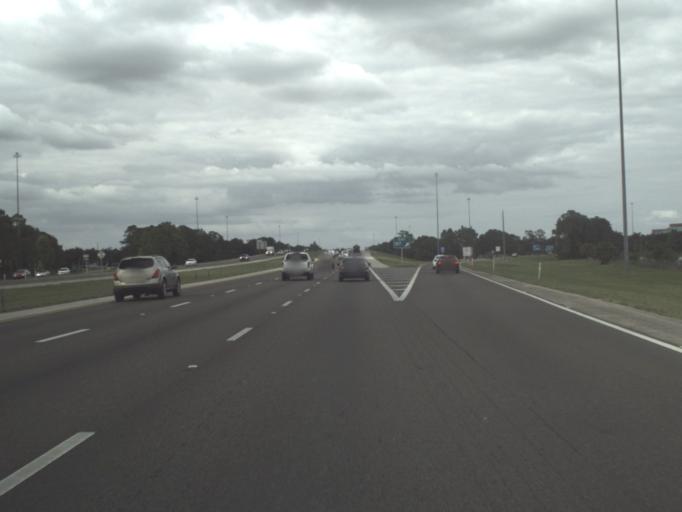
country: US
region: Florida
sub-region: Collier County
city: Vineyards
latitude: 26.2056
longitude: -81.7358
